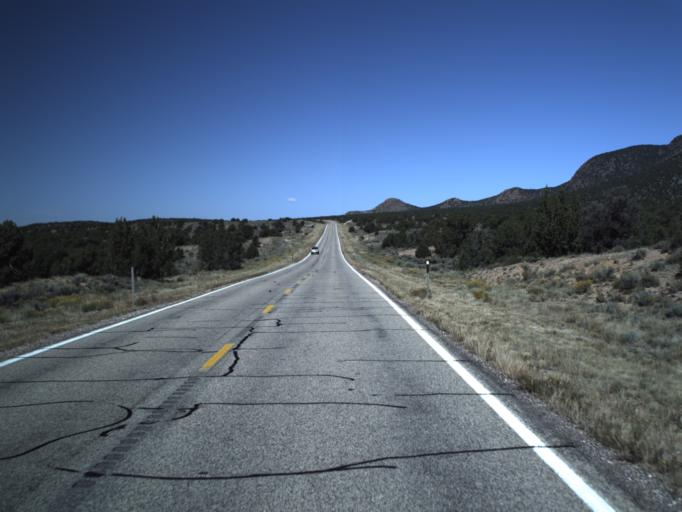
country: US
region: Utah
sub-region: Washington County
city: Enterprise
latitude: 37.6472
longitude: -113.4455
